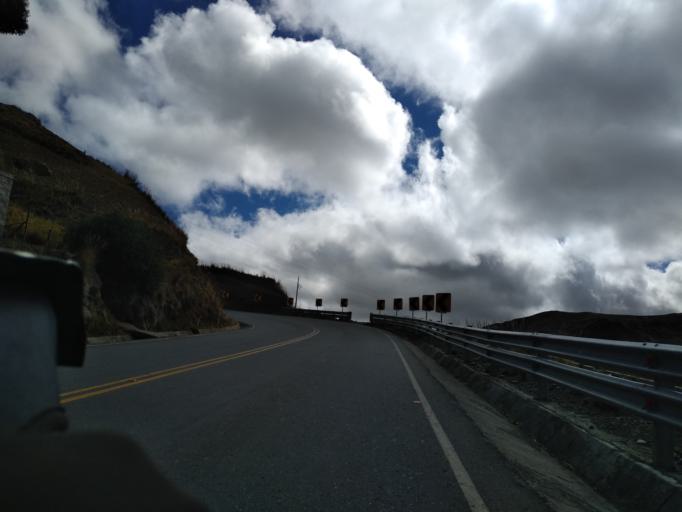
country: EC
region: Cotopaxi
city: Pujili
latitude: -0.9641
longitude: -78.9060
